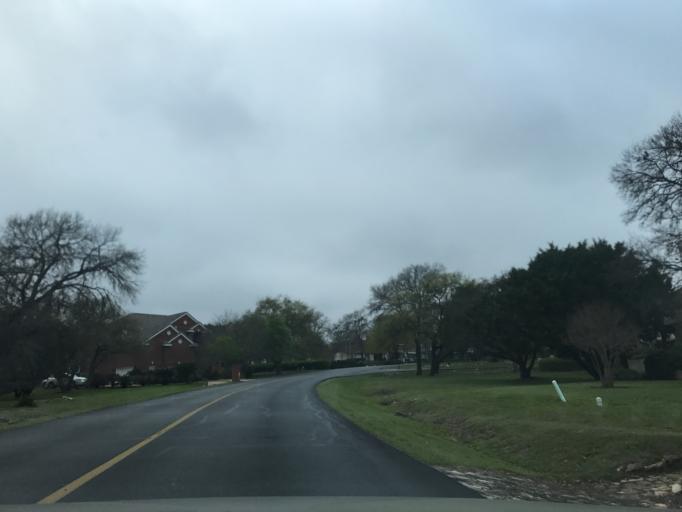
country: US
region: Texas
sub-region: Travis County
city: The Hills
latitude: 30.3391
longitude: -97.9900
